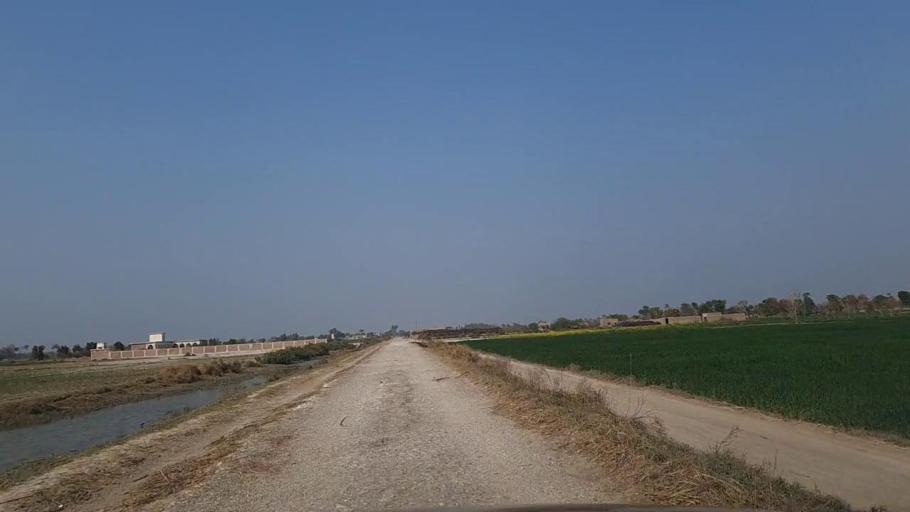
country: PK
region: Sindh
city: Daur
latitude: 26.4183
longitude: 68.4088
